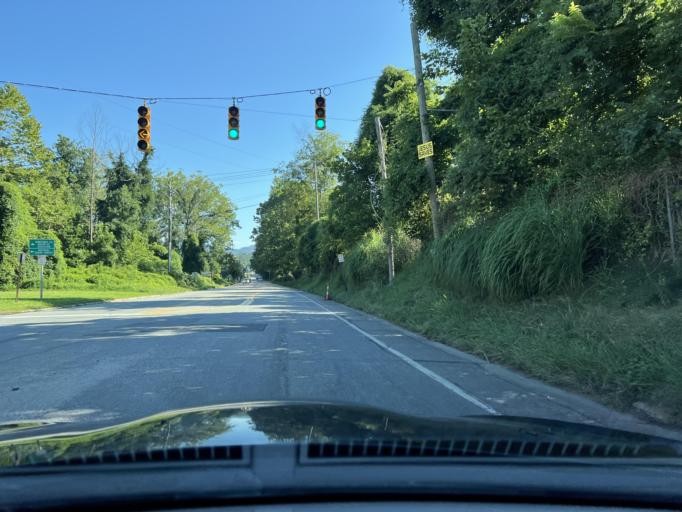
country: US
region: North Carolina
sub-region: Buncombe County
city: Asheville
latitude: 35.6085
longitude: -82.5772
